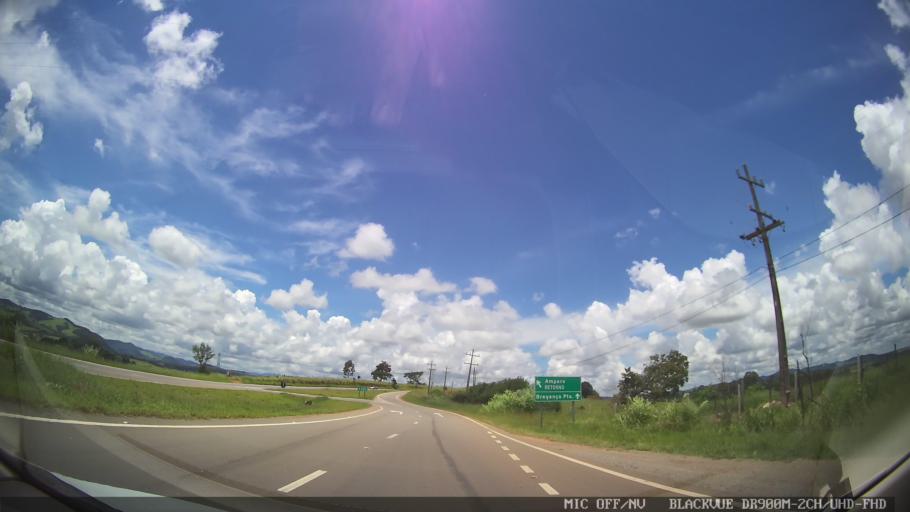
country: BR
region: Sao Paulo
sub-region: Braganca Paulista
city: Braganca Paulista
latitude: -22.8625
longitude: -46.6306
